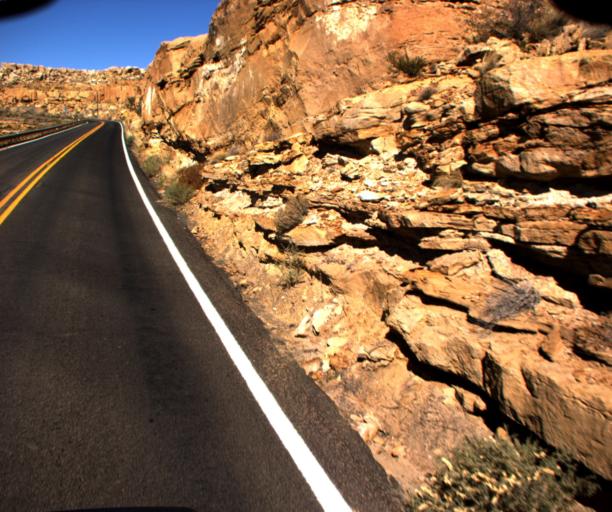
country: US
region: Arizona
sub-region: Navajo County
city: First Mesa
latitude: 35.8835
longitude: -110.6284
